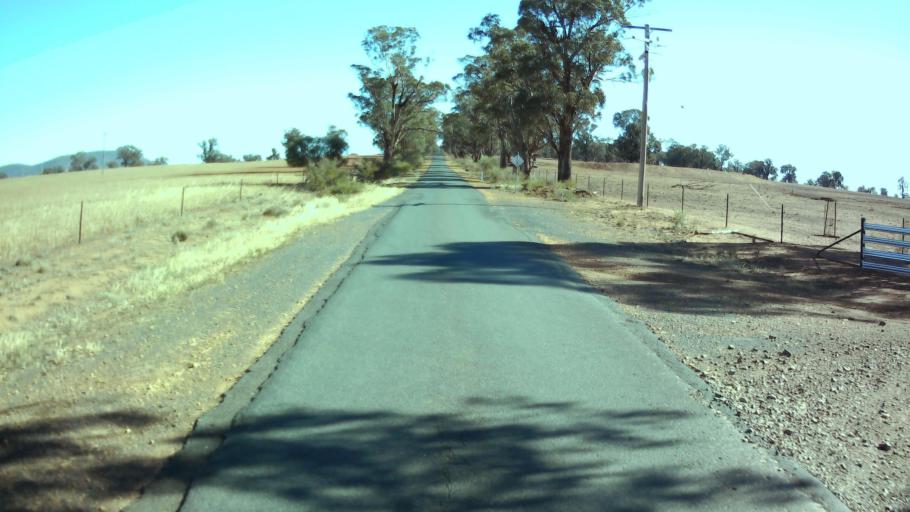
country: AU
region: New South Wales
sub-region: Weddin
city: Grenfell
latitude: -33.7911
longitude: 147.9574
